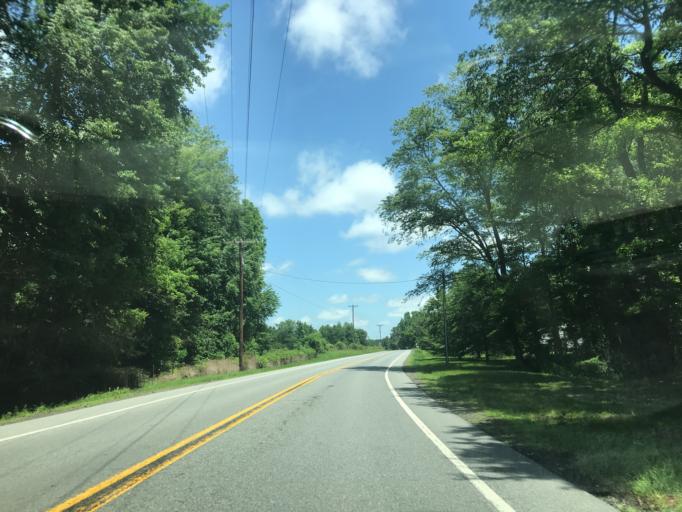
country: US
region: Maryland
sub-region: Caroline County
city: Federalsburg
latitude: 38.7323
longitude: -75.7297
